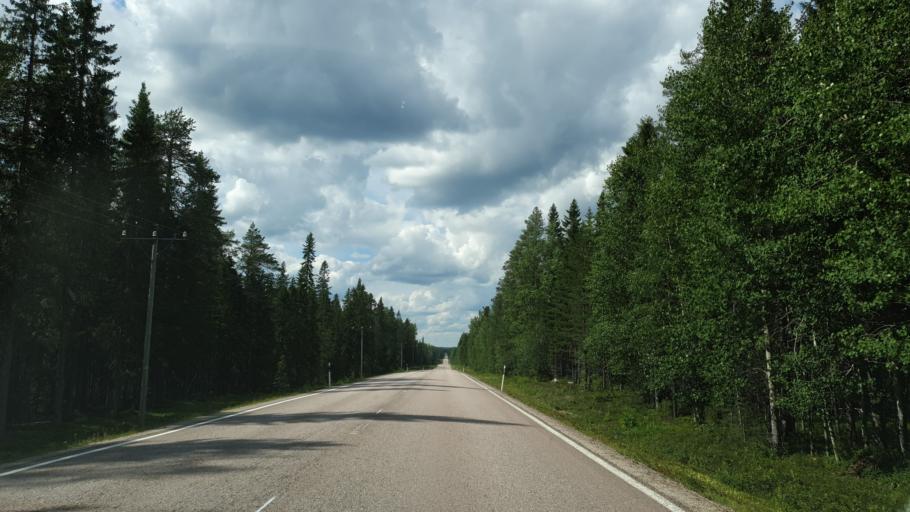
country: FI
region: Kainuu
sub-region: Kehys-Kainuu
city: Hyrynsalmi
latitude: 64.4625
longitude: 28.8557
